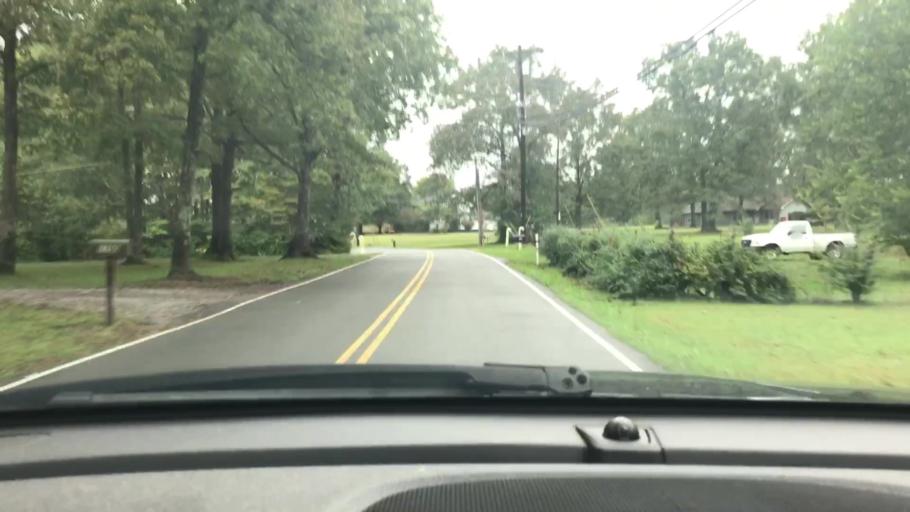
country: US
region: Tennessee
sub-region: Cheatham County
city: Kingston Springs
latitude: 36.1117
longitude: -87.1448
